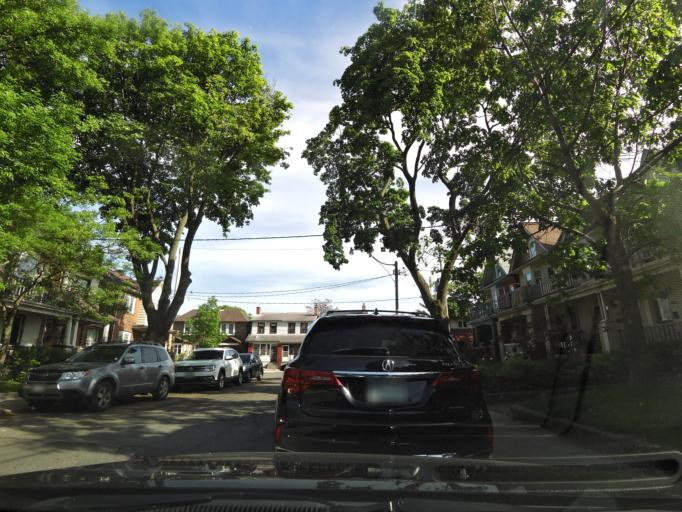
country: CA
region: Ontario
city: Toronto
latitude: 43.6582
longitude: -79.4812
